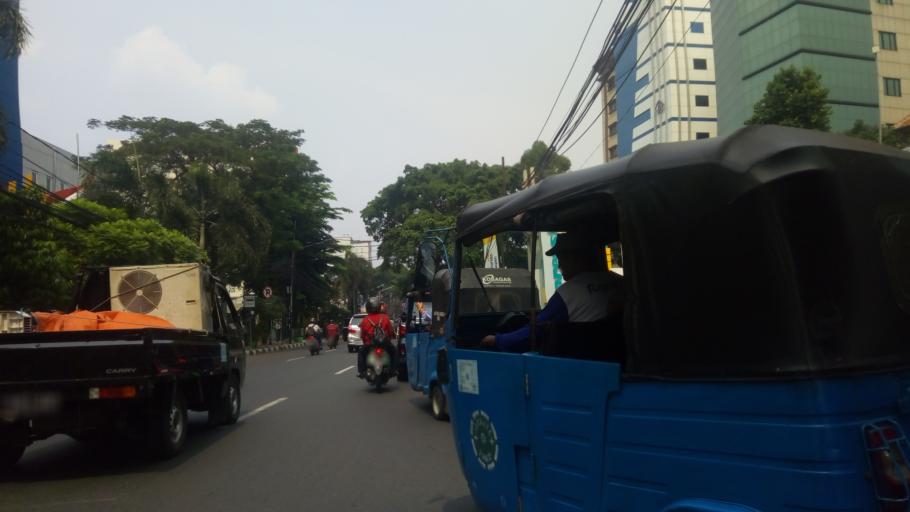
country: ID
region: Jakarta Raya
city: Jakarta
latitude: -6.1913
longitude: 106.8383
